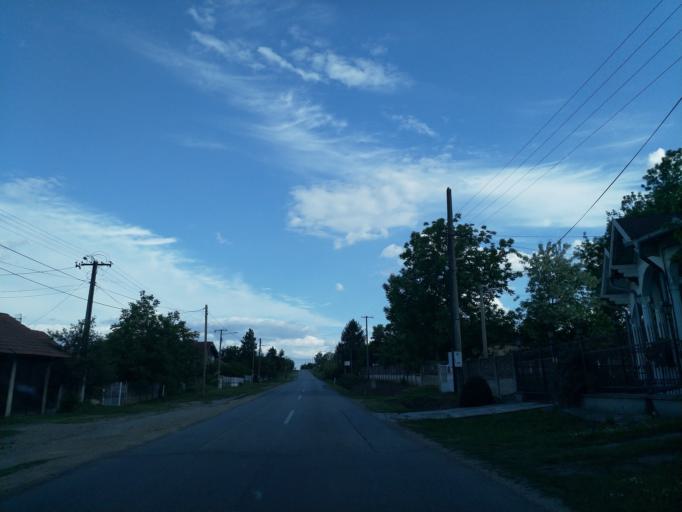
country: RS
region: Central Serbia
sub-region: Sumadijski Okrug
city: Lapovo
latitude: 44.1669
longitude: 21.0942
